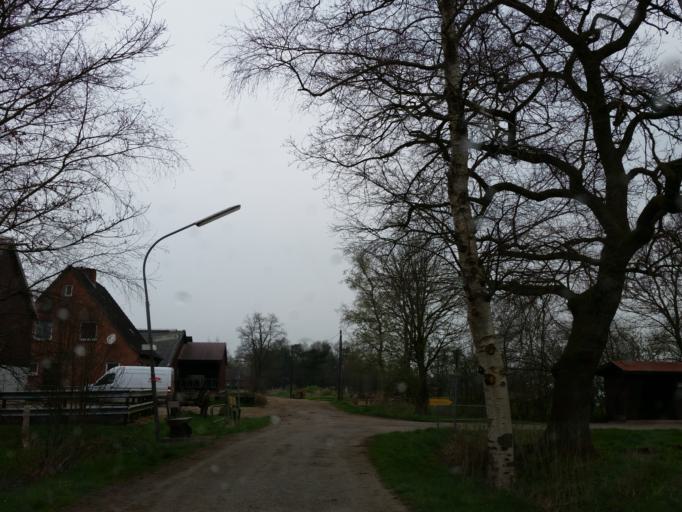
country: DE
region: Lower Saxony
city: Armstorf
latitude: 53.5838
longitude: 9.0100
